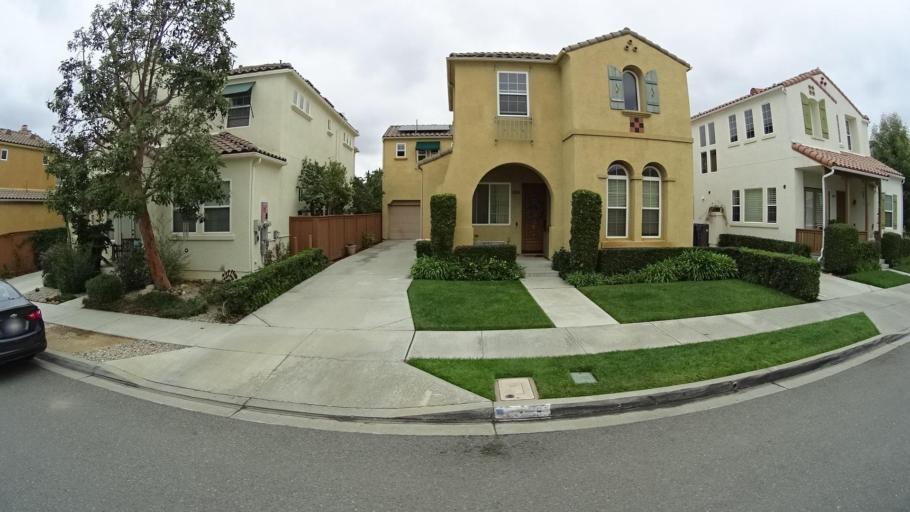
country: US
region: California
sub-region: San Diego County
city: Fairbanks Ranch
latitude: 33.0157
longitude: -117.1124
